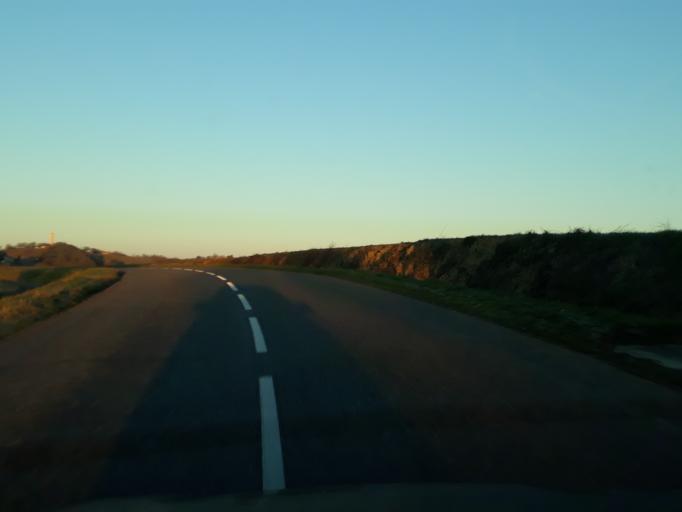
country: FR
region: Midi-Pyrenees
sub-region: Departement du Gers
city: Aubiet
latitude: 43.6004
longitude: 0.7159
